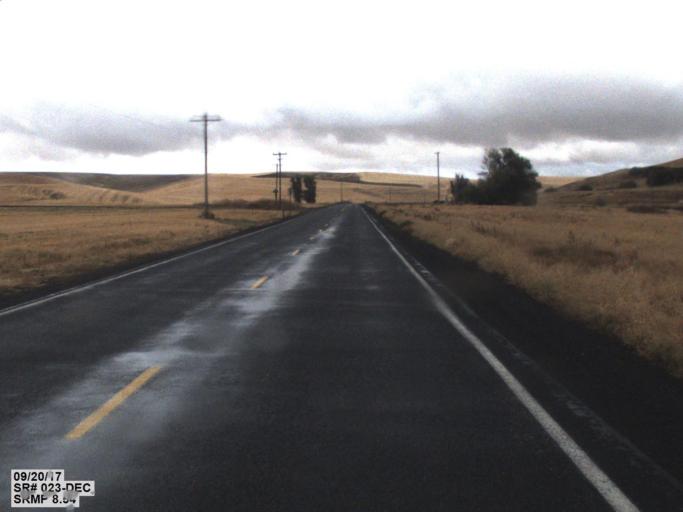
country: US
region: Washington
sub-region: Whitman County
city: Colfax
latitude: 47.0374
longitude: -117.5060
